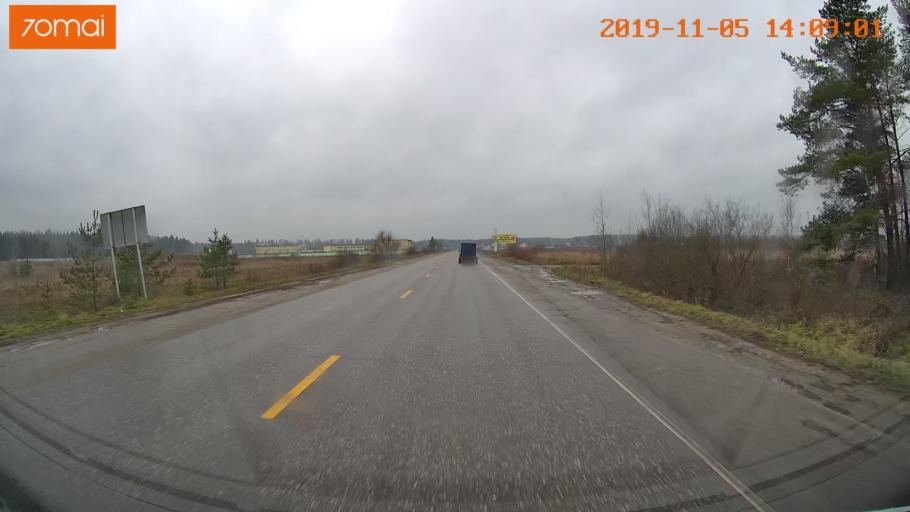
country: RU
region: Ivanovo
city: Kokhma
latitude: 56.9826
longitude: 41.0959
